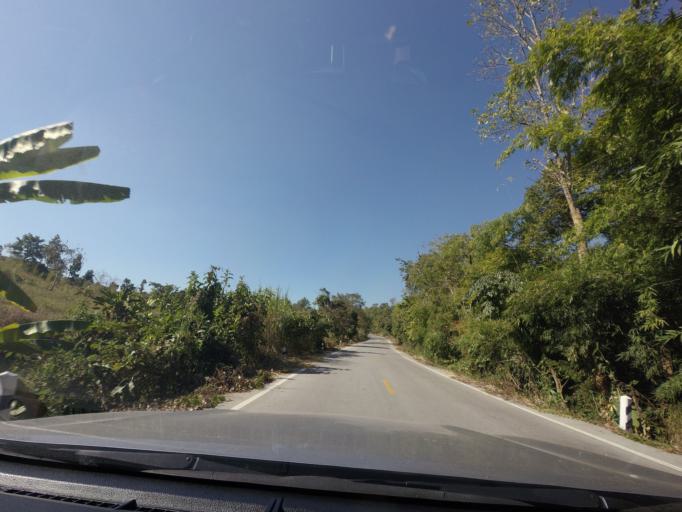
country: TH
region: Lampang
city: Chae Hom
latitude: 18.5599
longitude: 99.6262
